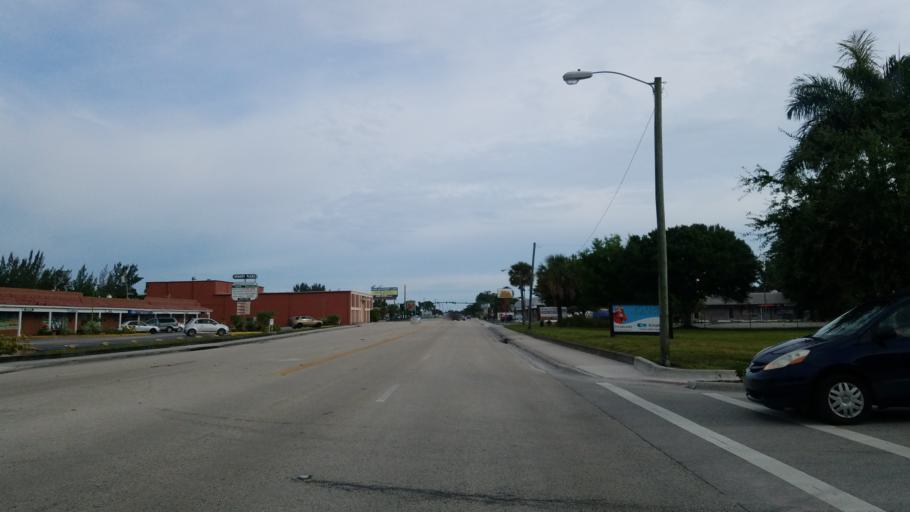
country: US
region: Florida
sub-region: Martin County
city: Port Salerno
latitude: 27.1660
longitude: -80.2197
